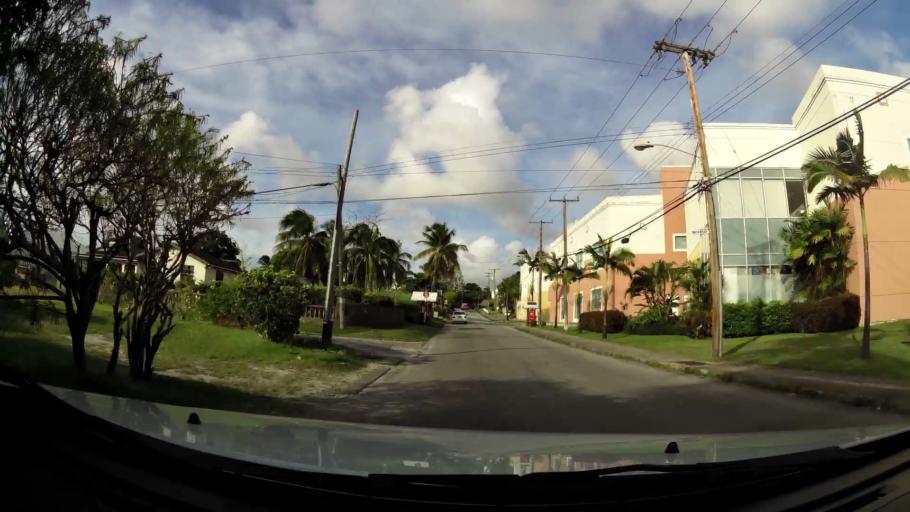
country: BB
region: Christ Church
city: Oistins
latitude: 13.0831
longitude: -59.5680
